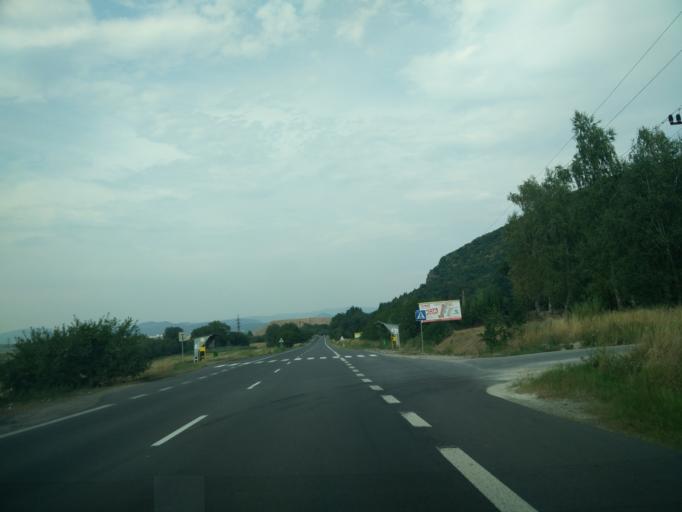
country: SK
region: Banskobystricky
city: Ziar nad Hronom
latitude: 48.5502
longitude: 18.8201
